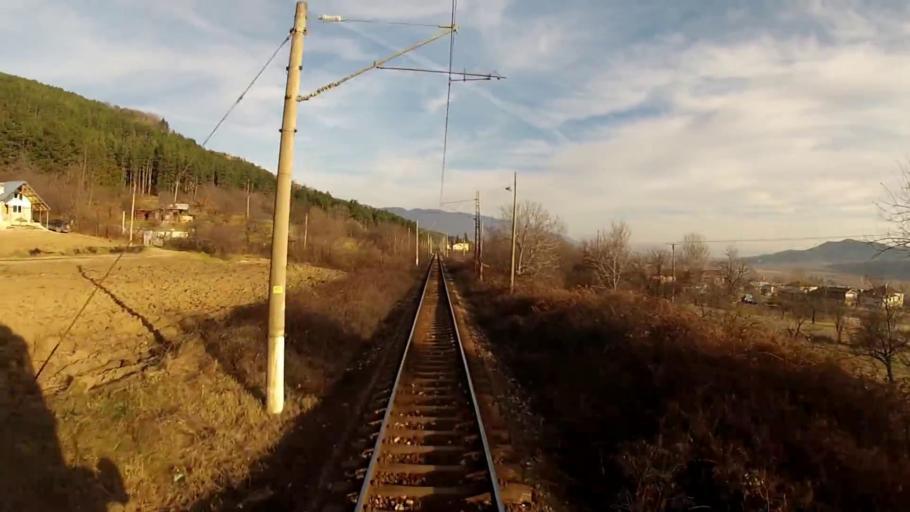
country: BG
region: Plovdiv
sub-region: Obshtina Karlovo
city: Klisura
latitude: 42.7218
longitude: 24.5866
